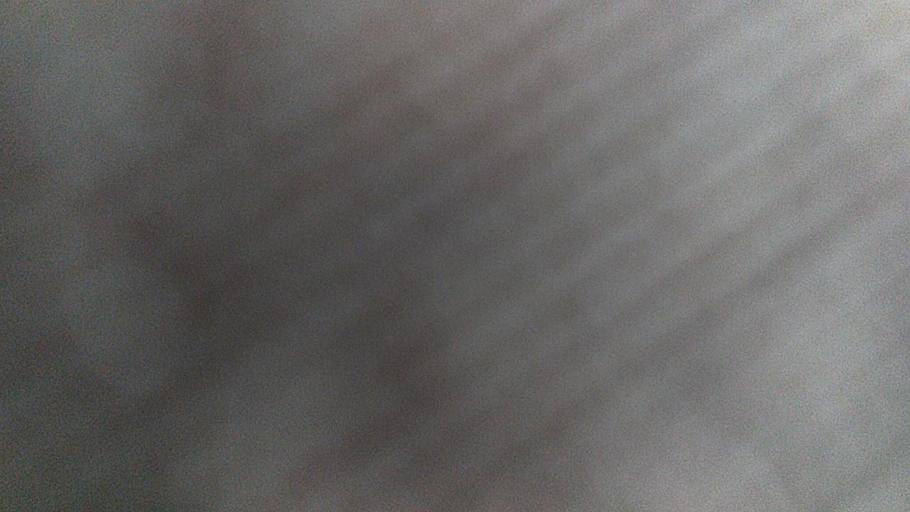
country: BO
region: La Paz
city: La Paz
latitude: -16.5366
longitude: -68.1352
